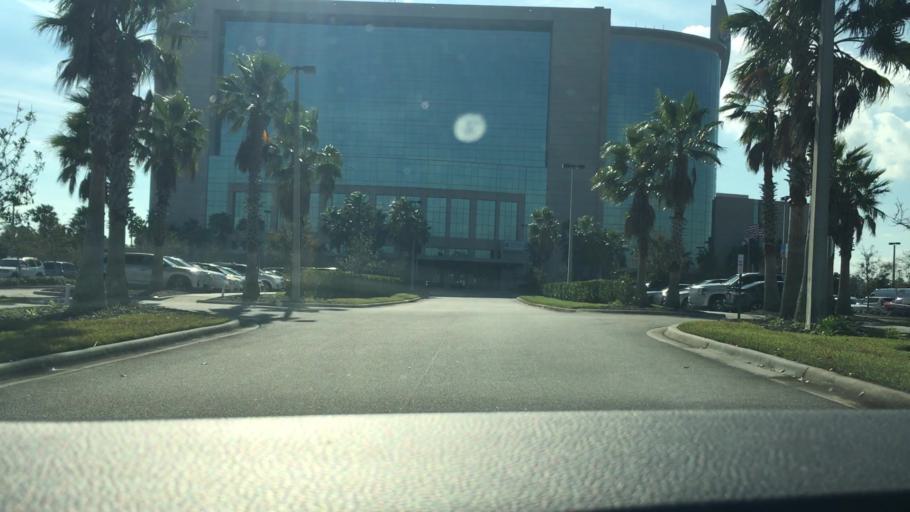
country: US
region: Florida
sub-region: Volusia County
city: Ormond Beach
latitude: 29.2451
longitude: -81.1087
